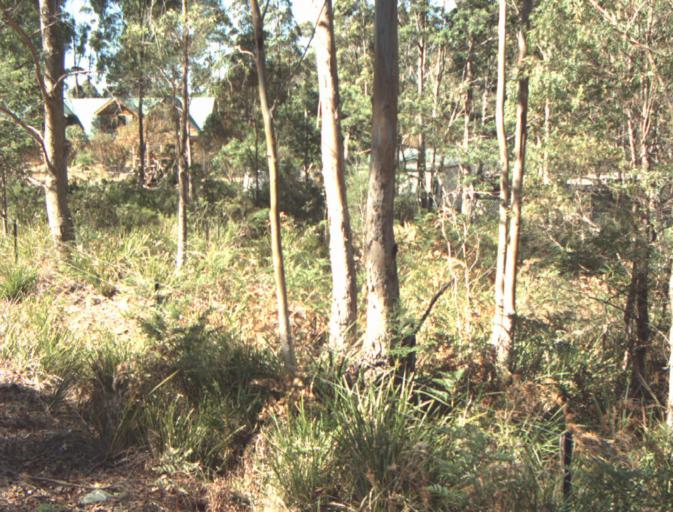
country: AU
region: Tasmania
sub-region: Launceston
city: Newstead
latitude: -41.3041
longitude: 147.3160
